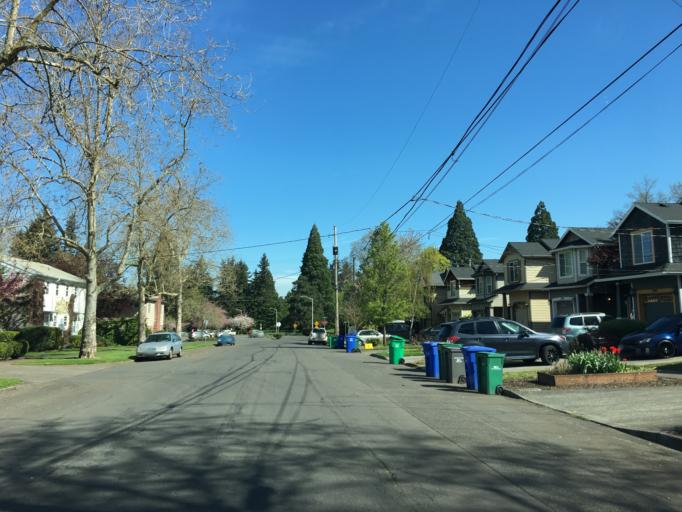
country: US
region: Oregon
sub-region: Multnomah County
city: Lents
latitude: 45.5364
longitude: -122.5894
